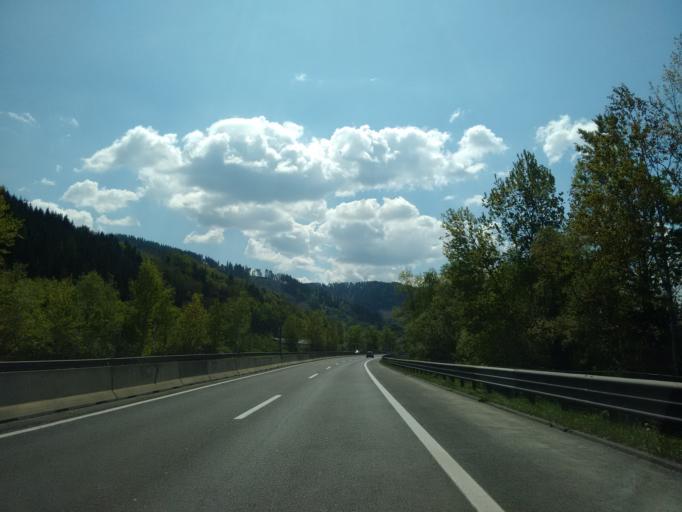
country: AT
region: Styria
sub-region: Politischer Bezirk Bruck-Muerzzuschlag
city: Oberaich
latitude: 47.4049
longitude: 15.1940
